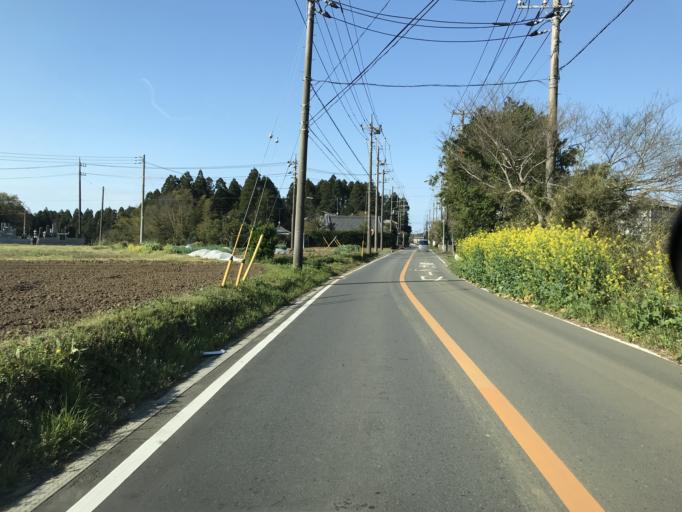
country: JP
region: Chiba
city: Omigawa
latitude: 35.8424
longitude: 140.5599
